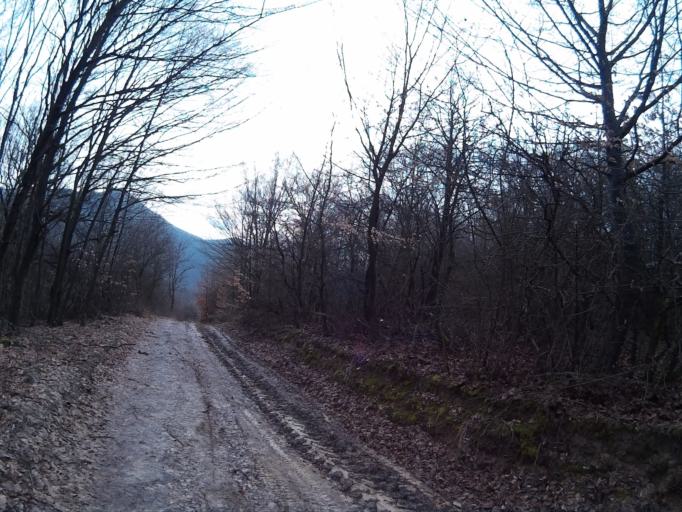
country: HU
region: Borsod-Abauj-Zemplen
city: Satoraljaujhely
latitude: 48.4088
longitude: 21.5988
